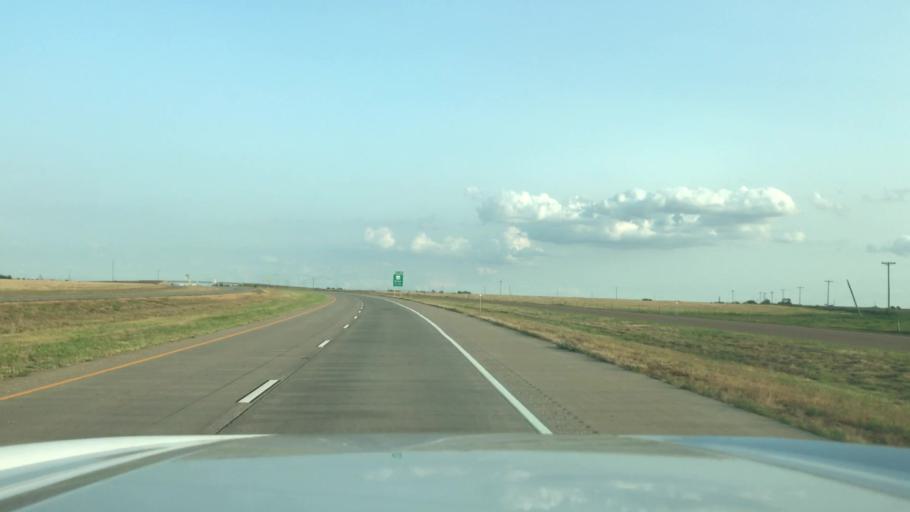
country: US
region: Texas
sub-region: Swisher County
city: Tulia
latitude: 34.3816
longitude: -101.7761
